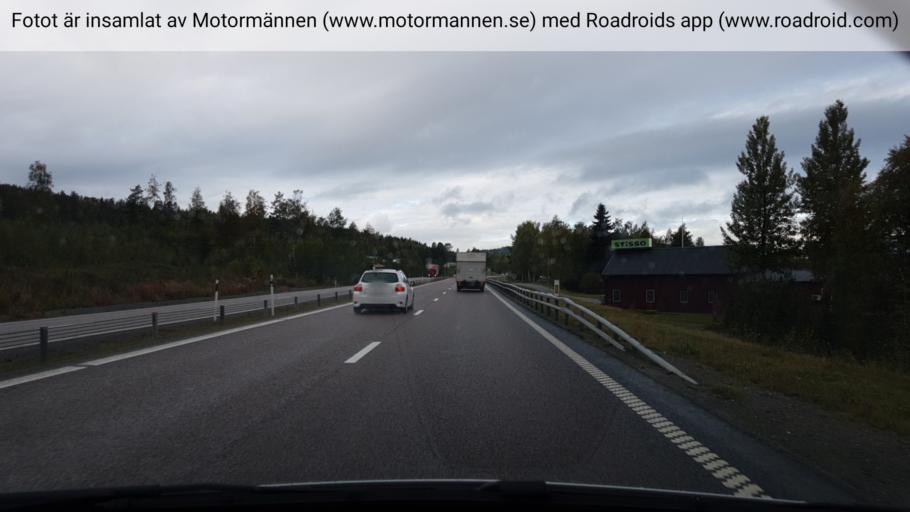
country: SE
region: Vaesternorrland
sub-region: OErnskoeldsviks Kommun
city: Ornskoldsvik
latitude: 63.3052
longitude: 18.7602
